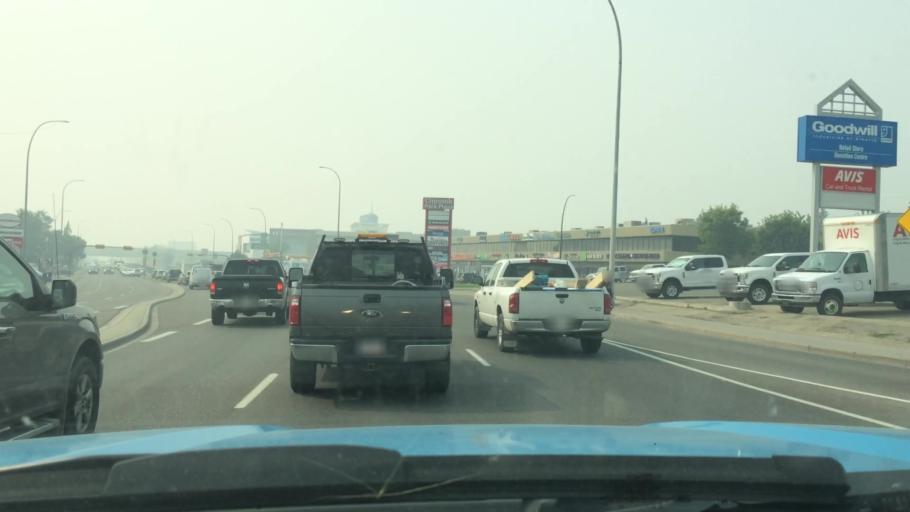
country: CA
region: Alberta
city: Calgary
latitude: 51.0023
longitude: -114.0698
